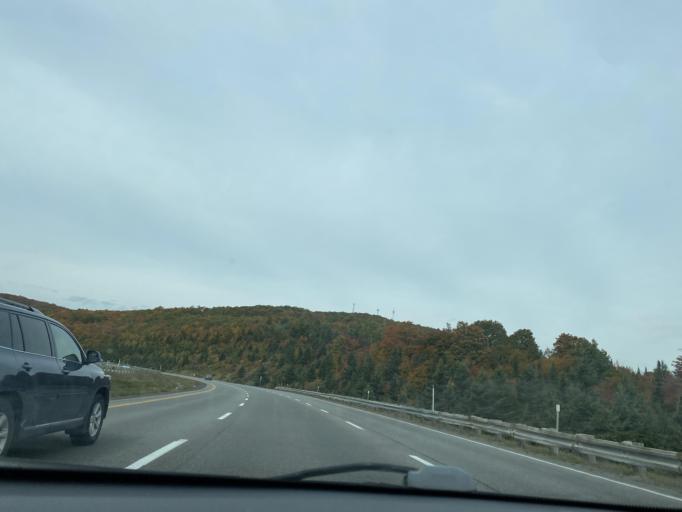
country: CA
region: Quebec
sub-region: Laurentides
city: Sainte-Adele
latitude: 45.9779
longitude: -74.1609
